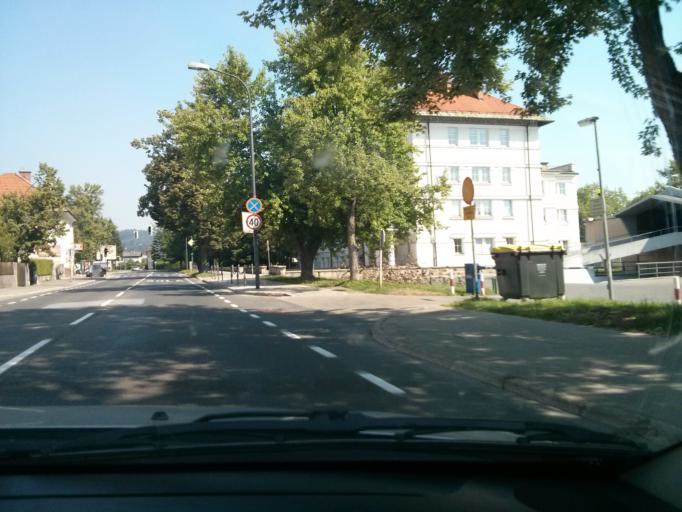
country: SI
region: Ljubljana
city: Ljubljana
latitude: 46.0731
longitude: 14.4766
